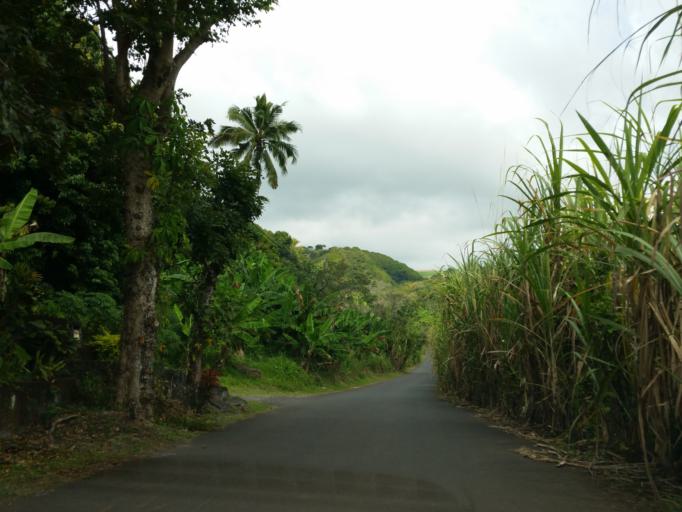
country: RE
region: Reunion
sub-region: Reunion
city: Sainte-Suzanne
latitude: -20.9193
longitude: 55.6125
